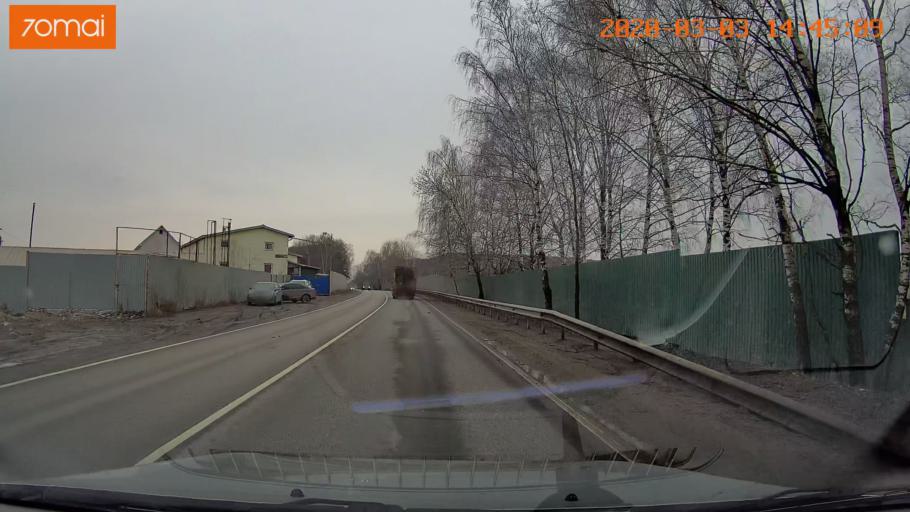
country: RU
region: Moskovskaya
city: Korenevo
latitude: 55.7004
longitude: 38.0416
